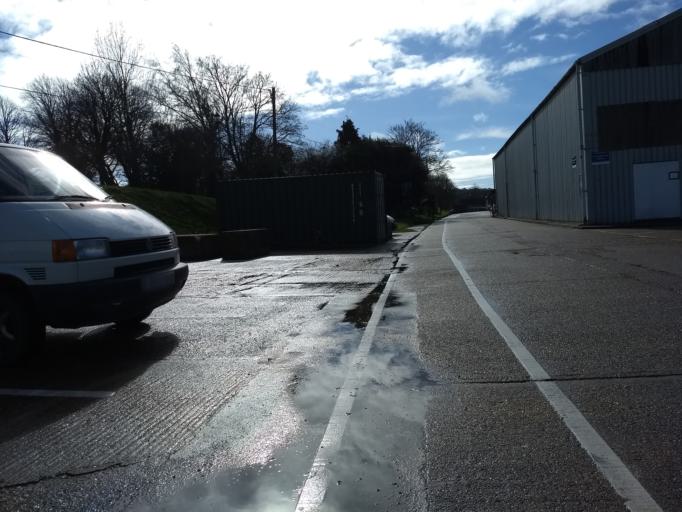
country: GB
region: England
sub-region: Isle of Wight
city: Newport
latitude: 50.7054
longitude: -1.2907
